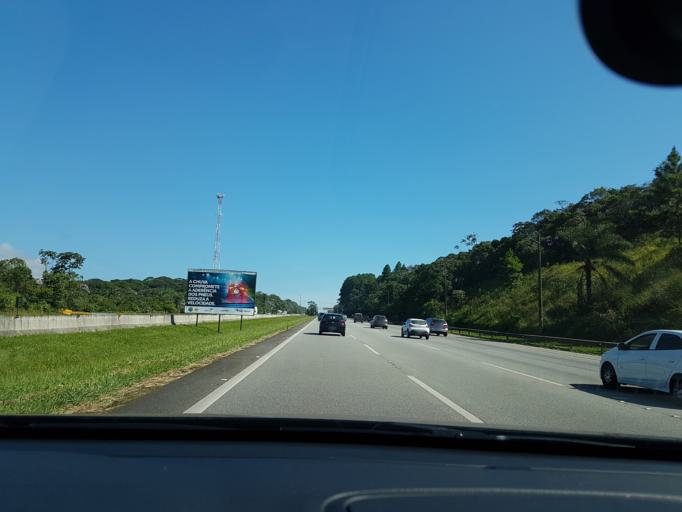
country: BR
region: Sao Paulo
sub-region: Sao Bernardo Do Campo
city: Sao Bernardo do Campo
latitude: -23.8327
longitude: -46.5796
